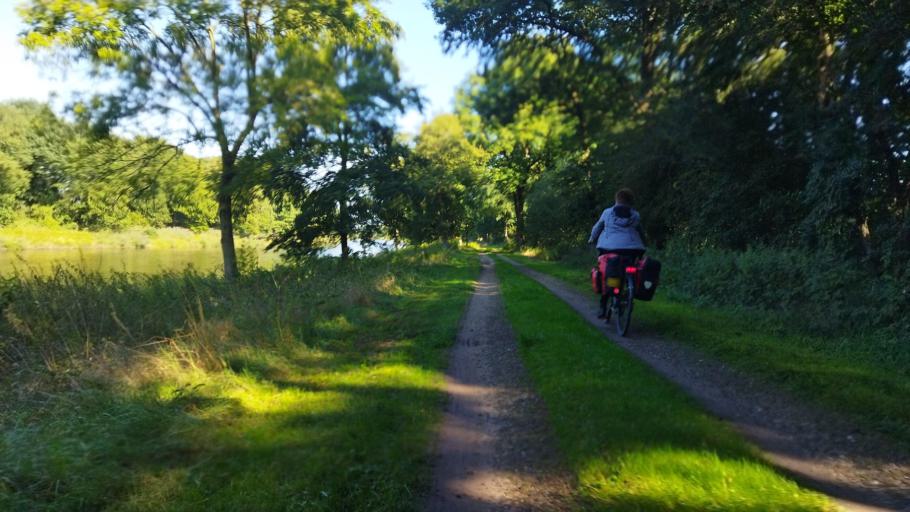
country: DE
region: Lower Saxony
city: Haren
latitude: 52.7703
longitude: 7.2563
